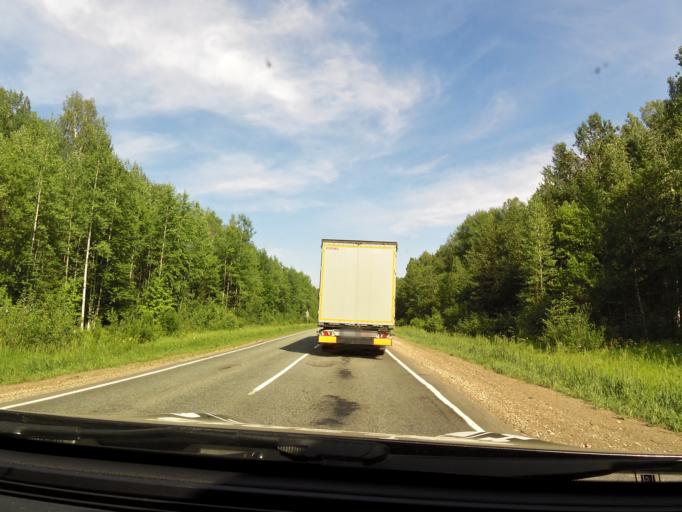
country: RU
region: Kirov
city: Belaya Kholunitsa
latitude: 58.8293
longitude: 50.6392
